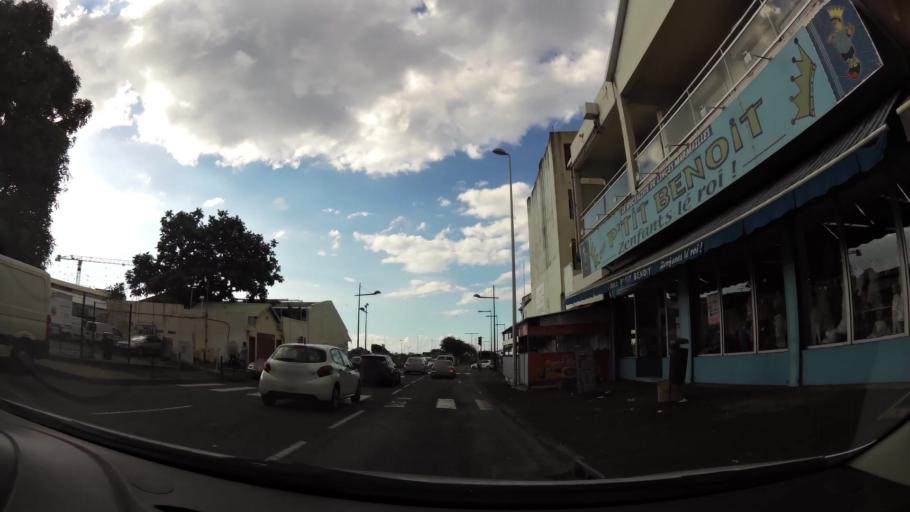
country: RE
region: Reunion
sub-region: Reunion
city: Saint-Denis
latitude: -20.8809
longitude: 55.4573
